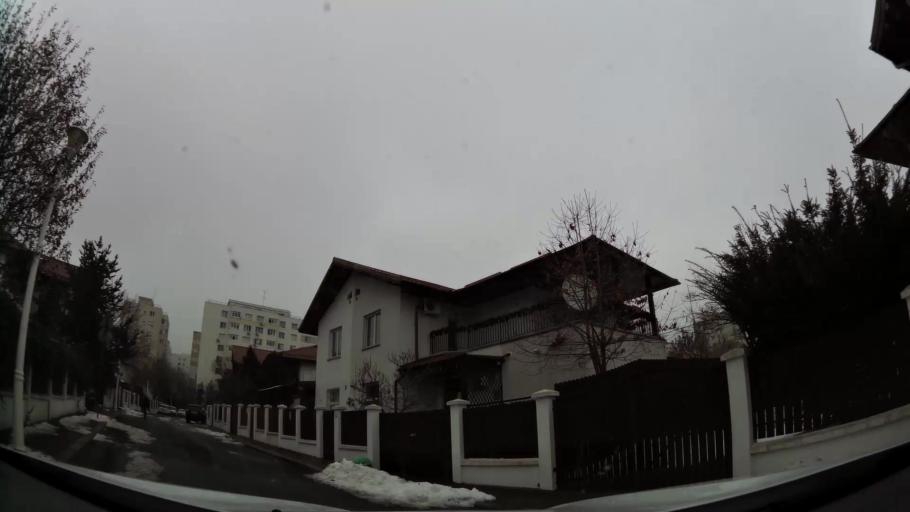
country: RO
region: Ilfov
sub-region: Comuna Popesti-Leordeni
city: Popesti-Leordeni
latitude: 44.4079
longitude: 26.1699
